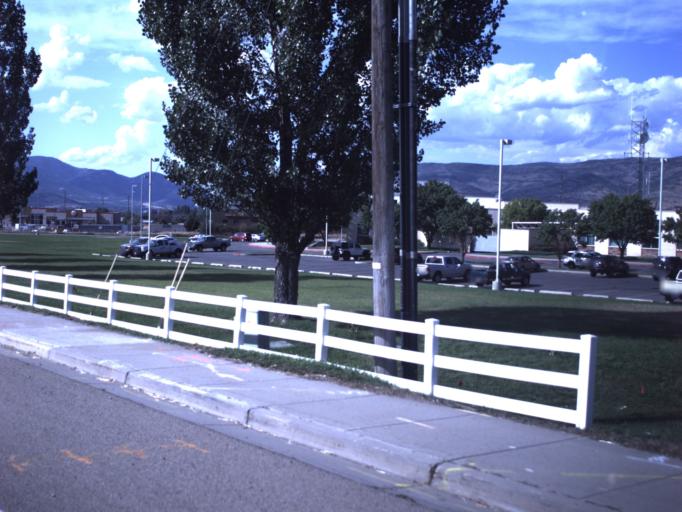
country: US
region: Utah
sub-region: Wasatch County
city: Heber
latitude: 40.4894
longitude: -111.4096
